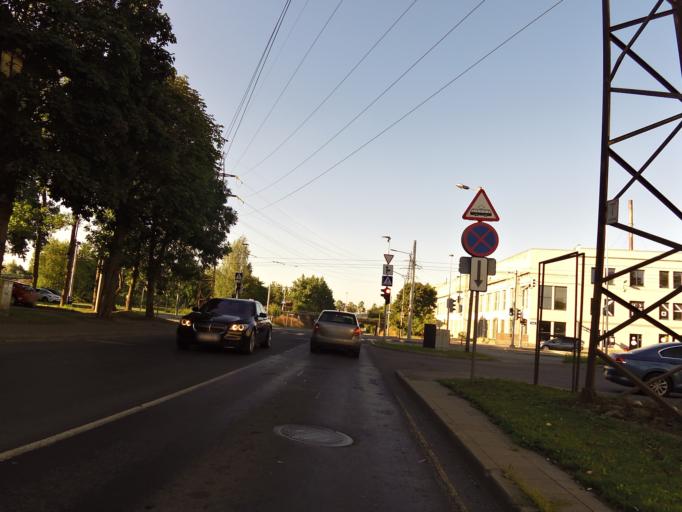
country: EE
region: Harju
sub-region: Tallinna linn
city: Tallinn
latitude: 59.4487
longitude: 24.7124
